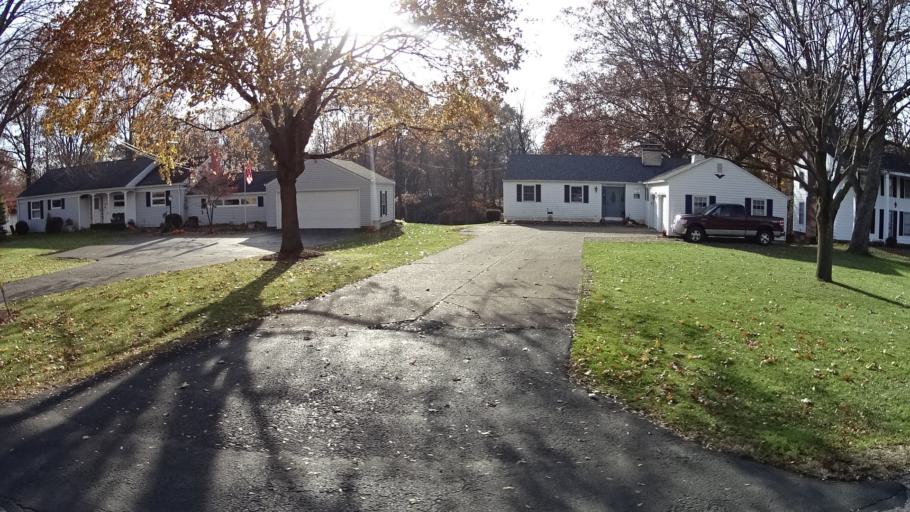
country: US
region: Ohio
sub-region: Lorain County
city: Elyria
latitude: 41.3509
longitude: -82.0972
